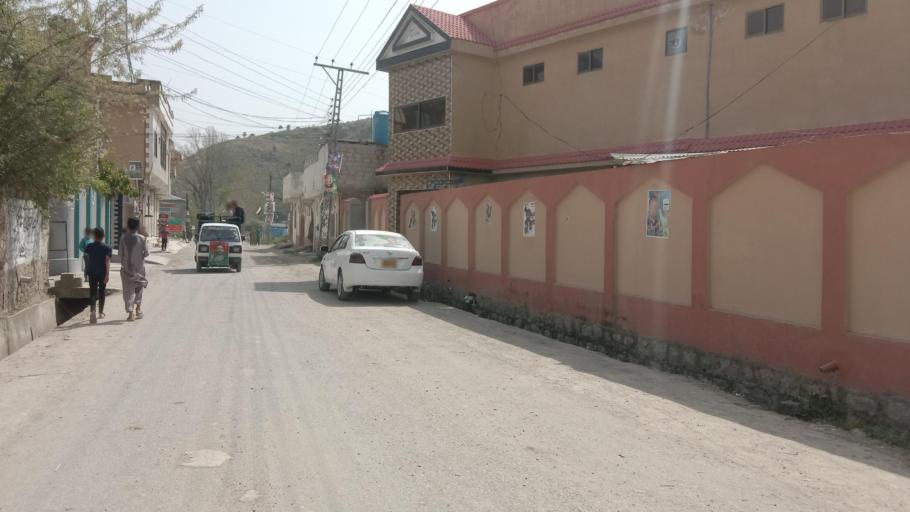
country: PK
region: Khyber Pakhtunkhwa
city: Abbottabad
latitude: 34.1558
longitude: 73.2598
